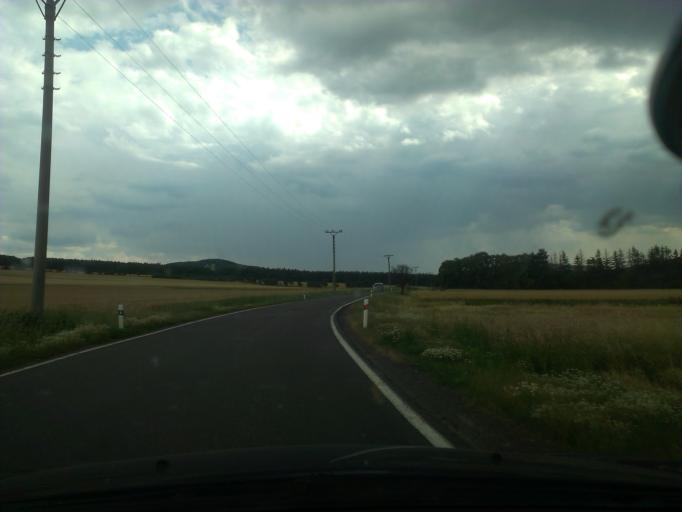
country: CZ
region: South Moravian
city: Velka nad Velickou
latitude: 48.8499
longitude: 17.5224
